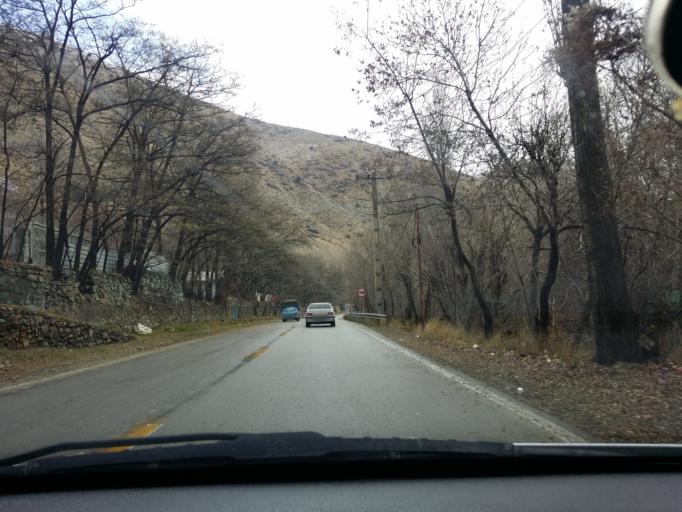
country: IR
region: Tehran
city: Tajrish
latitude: 36.0252
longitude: 51.2519
